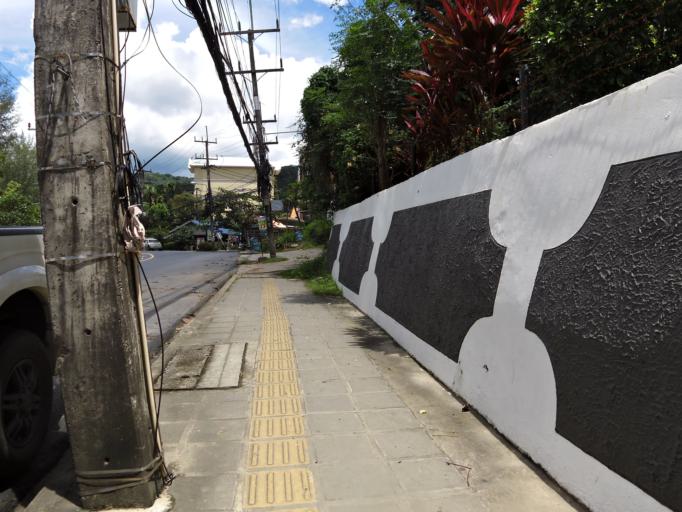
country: TH
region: Phuket
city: Ban Karon
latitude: 7.8521
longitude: 98.2949
